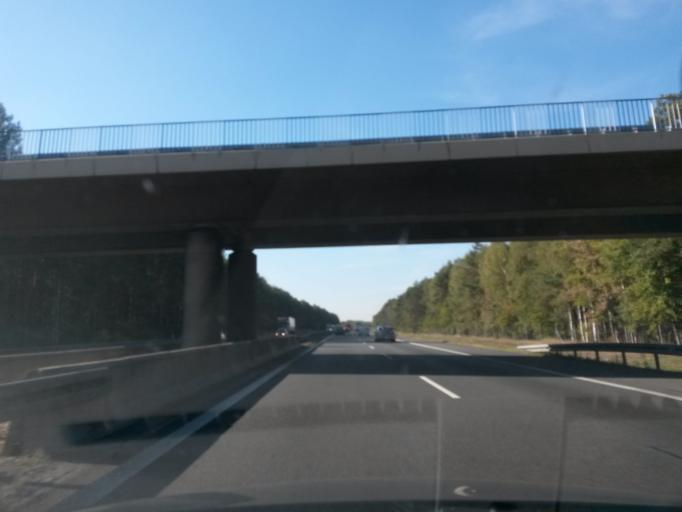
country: PL
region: Opole Voivodeship
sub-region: Powiat opolski
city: Proszkow
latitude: 50.5841
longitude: 17.8245
